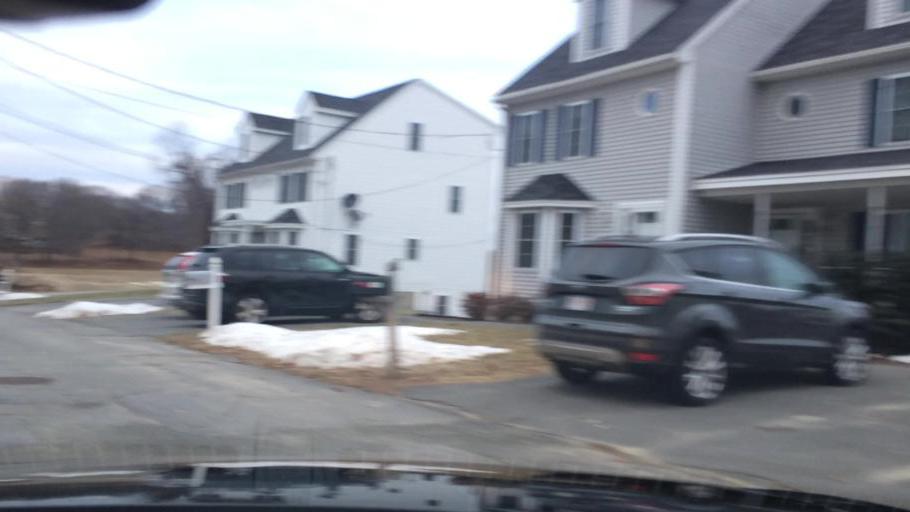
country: US
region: Massachusetts
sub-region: Essex County
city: North Andover
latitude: 42.7349
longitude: -71.1254
